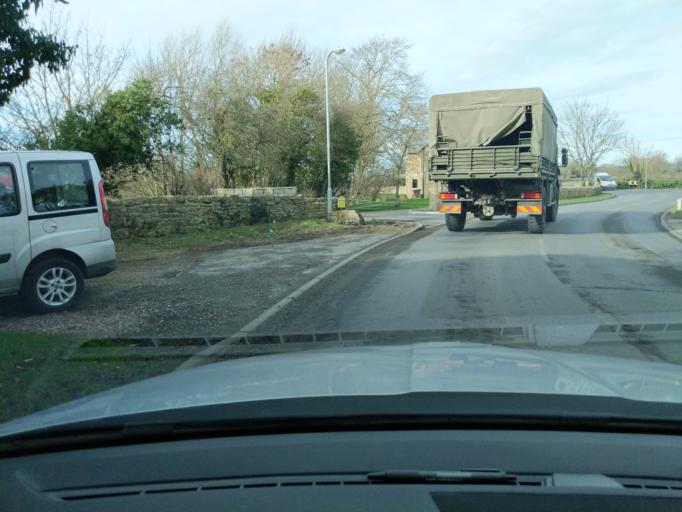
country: GB
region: England
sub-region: North Yorkshire
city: Catterick
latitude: 54.3929
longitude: -1.6702
